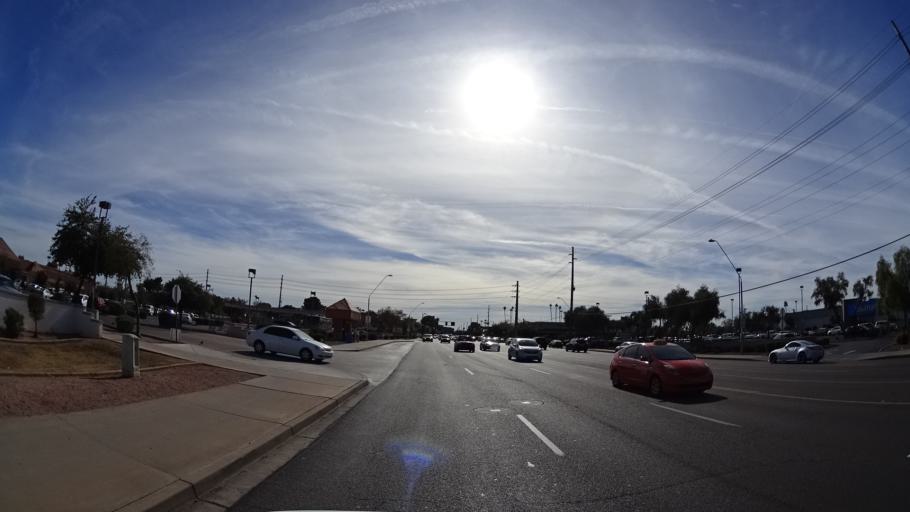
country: US
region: Arizona
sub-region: Maricopa County
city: Tempe Junction
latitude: 33.3944
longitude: -111.9262
